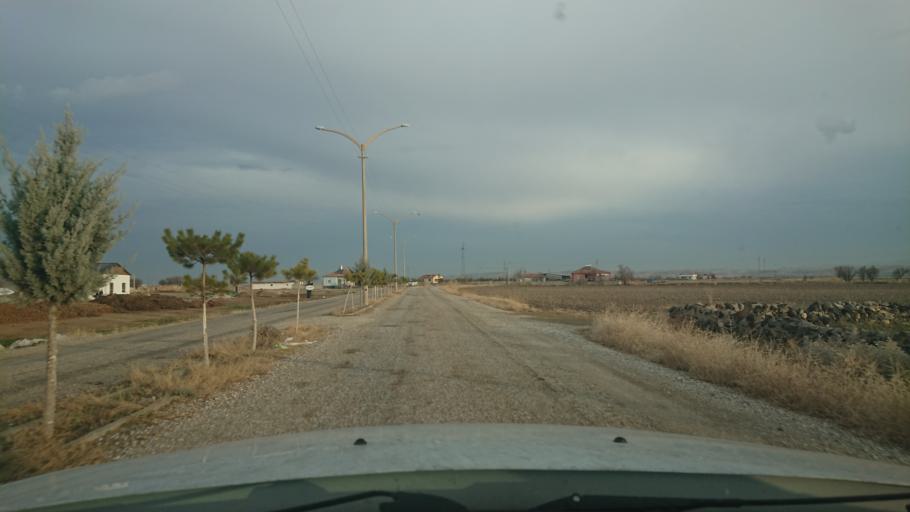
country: TR
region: Aksaray
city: Yesilova
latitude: 38.4217
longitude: 33.8345
